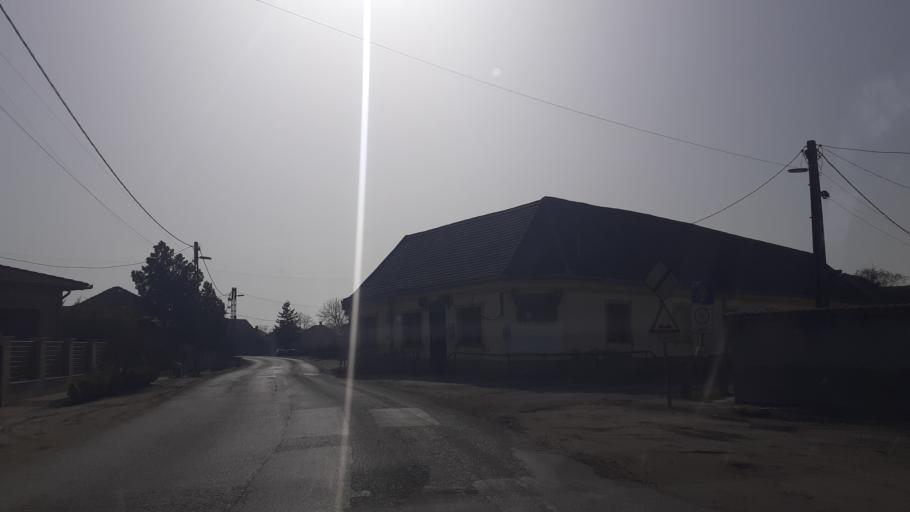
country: HU
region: Pest
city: Bugyi
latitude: 47.2212
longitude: 19.1465
